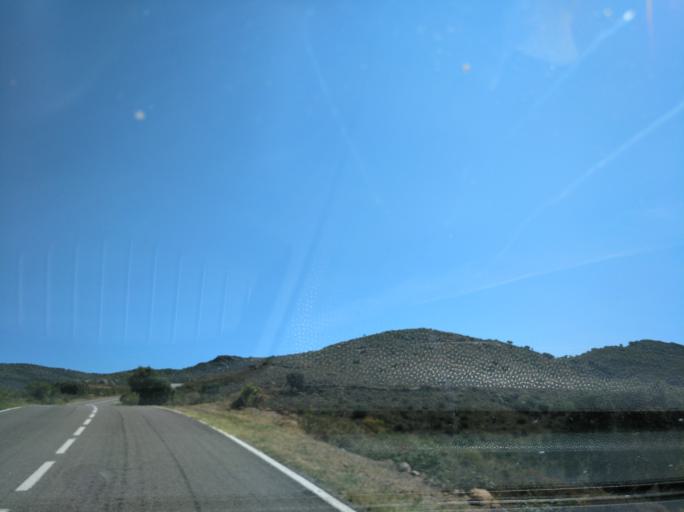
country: ES
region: Catalonia
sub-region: Provincia de Girona
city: Pau
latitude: 42.3369
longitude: 3.1228
